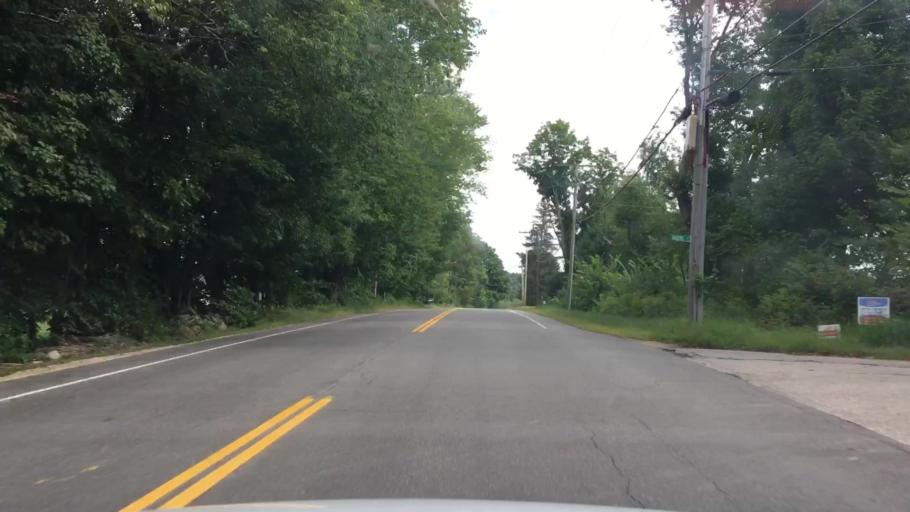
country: US
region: New Hampshire
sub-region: Strafford County
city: Madbury
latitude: 43.2002
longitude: -70.9572
